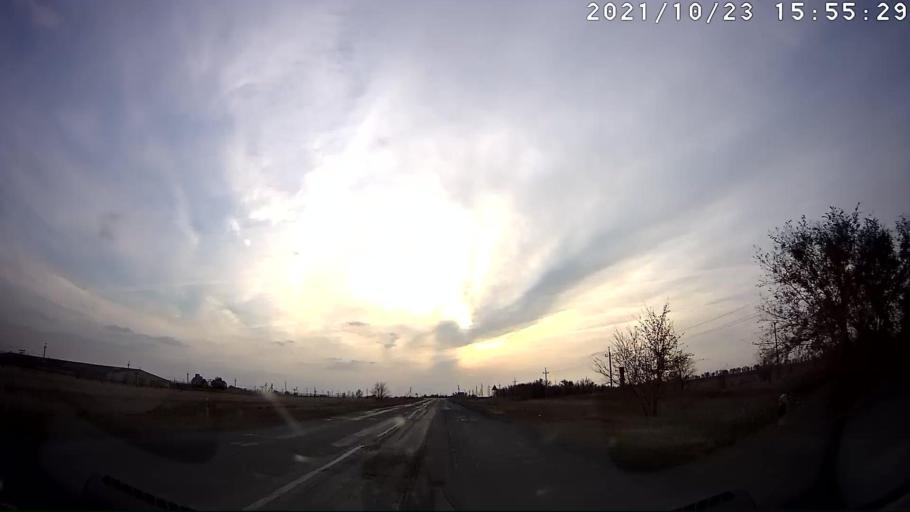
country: RU
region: Kalmykiya
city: Sadovoye
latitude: 47.9682
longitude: 43.9635
